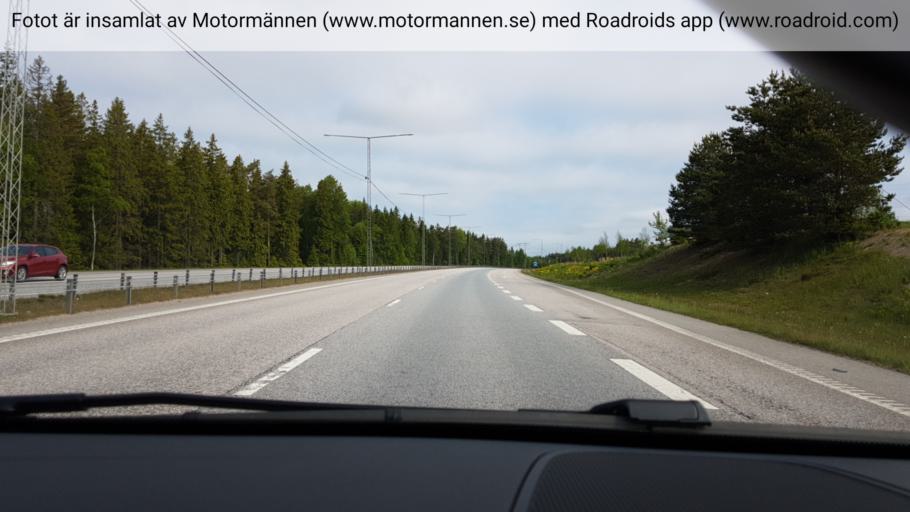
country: SE
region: Stockholm
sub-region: Haninge Kommun
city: Haninge
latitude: 59.1478
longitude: 18.1580
